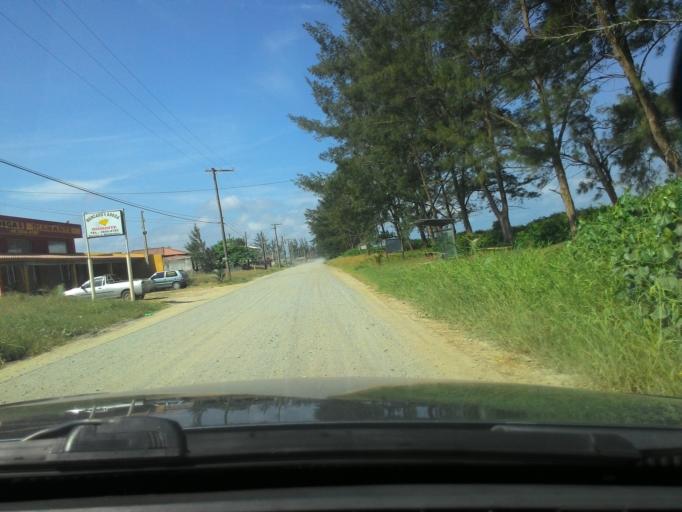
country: BR
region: Sao Paulo
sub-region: Iguape
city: Iguape
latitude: -24.8467
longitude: -47.6899
